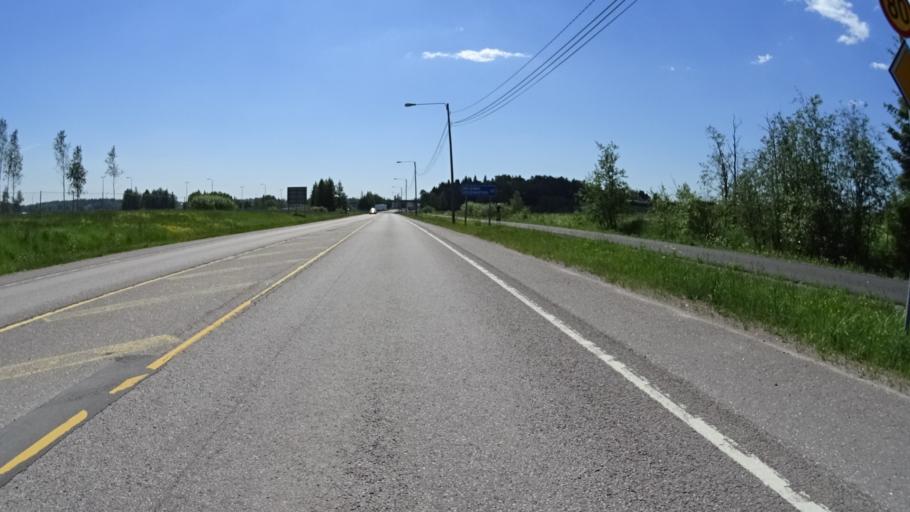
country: FI
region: Uusimaa
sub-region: Helsinki
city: Nurmijaervi
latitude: 60.3532
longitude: 24.8069
